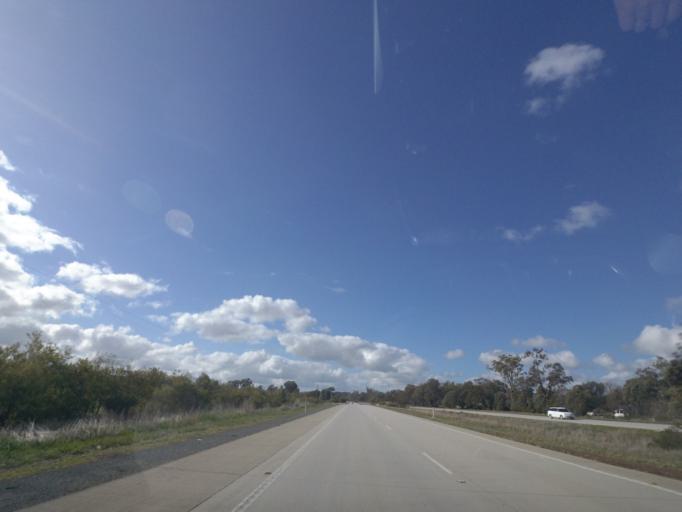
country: AU
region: New South Wales
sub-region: Greater Hume Shire
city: Holbrook
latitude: -35.9091
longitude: 147.1565
